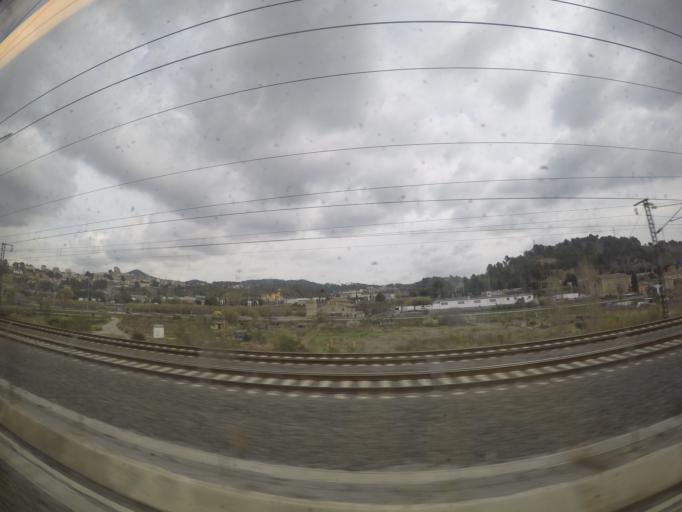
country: ES
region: Catalonia
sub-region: Provincia de Barcelona
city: Palleja
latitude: 41.4291
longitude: 2.0025
